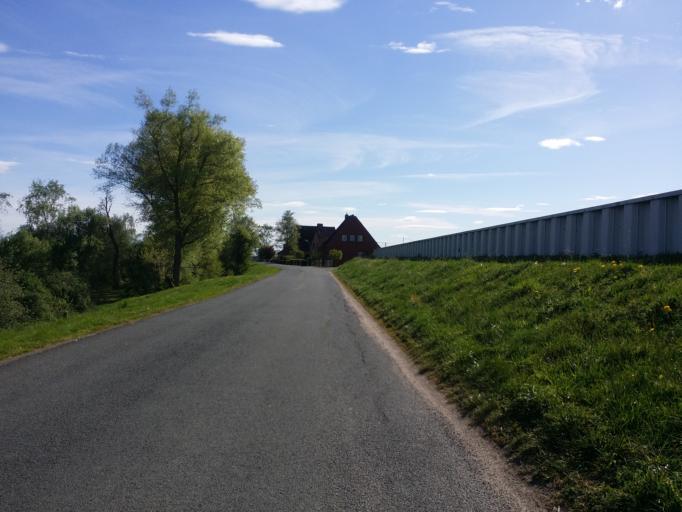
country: DE
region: Lower Saxony
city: Lemwerder
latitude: 53.1569
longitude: 8.6306
